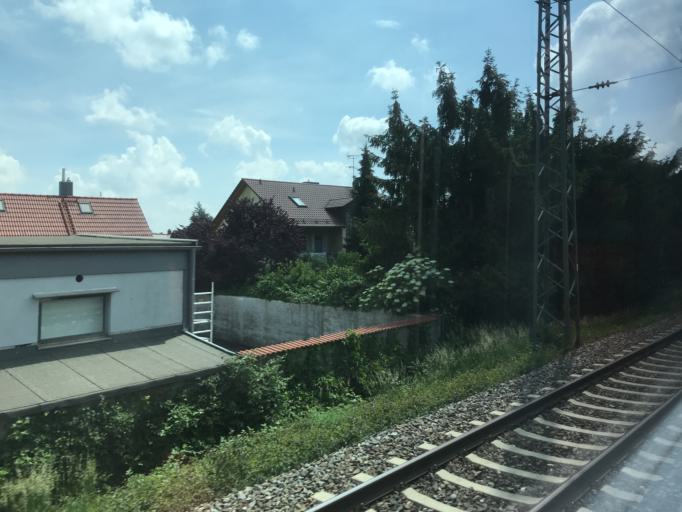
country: DE
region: Bavaria
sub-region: Swabia
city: Augsburg
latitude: 48.3842
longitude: 10.8712
